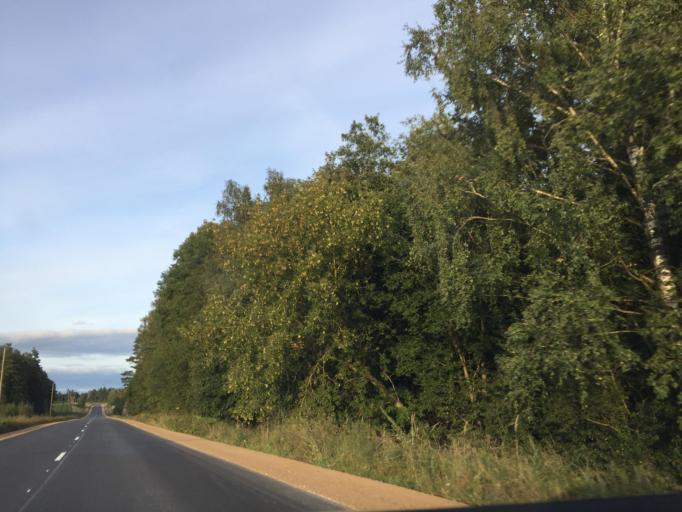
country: LV
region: Viesite
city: Viesite
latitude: 56.3660
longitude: 25.6323
